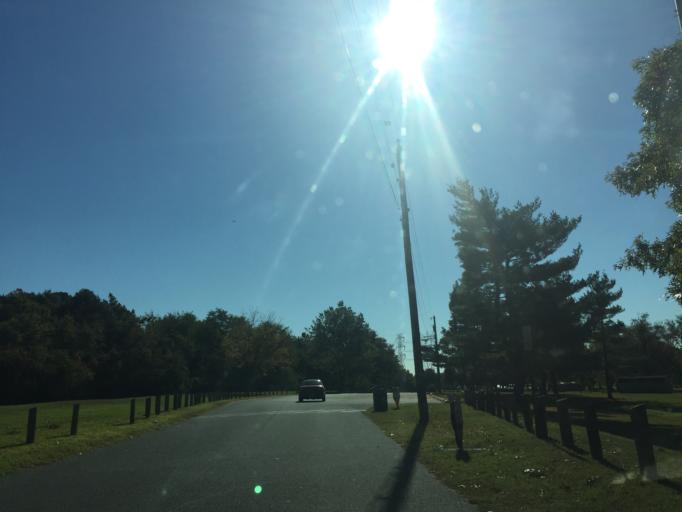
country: US
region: Maryland
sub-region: Baltimore County
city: Dundalk
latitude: 39.2542
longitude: -76.5055
